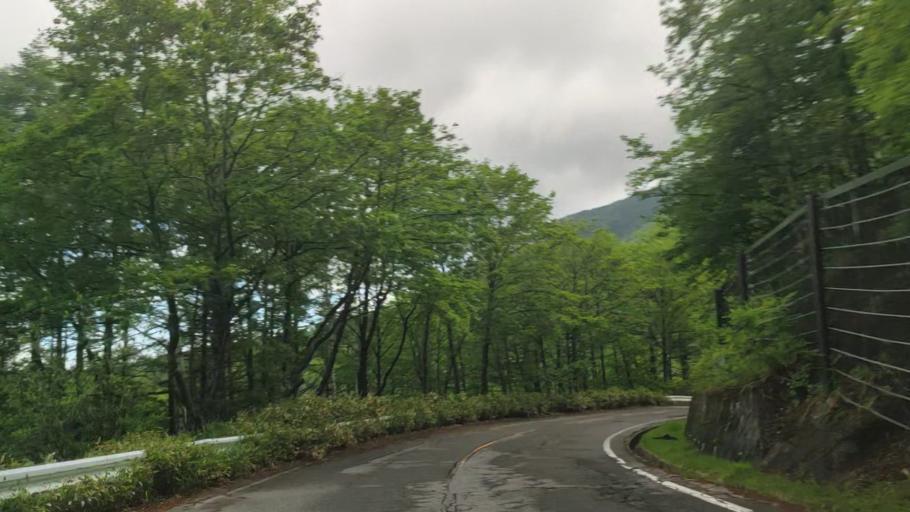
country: JP
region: Nagano
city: Chino
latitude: 36.0938
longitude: 138.2735
